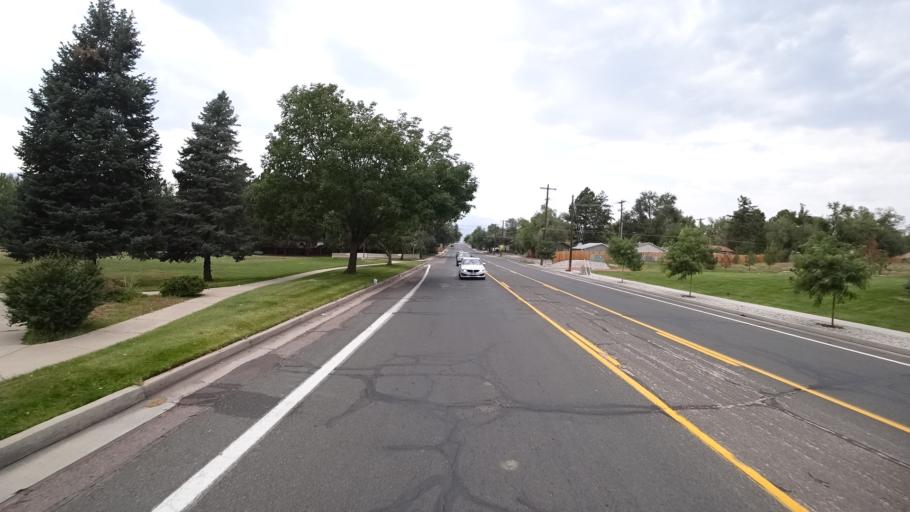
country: US
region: Colorado
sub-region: El Paso County
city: Colorado Springs
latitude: 38.8449
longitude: -104.7843
